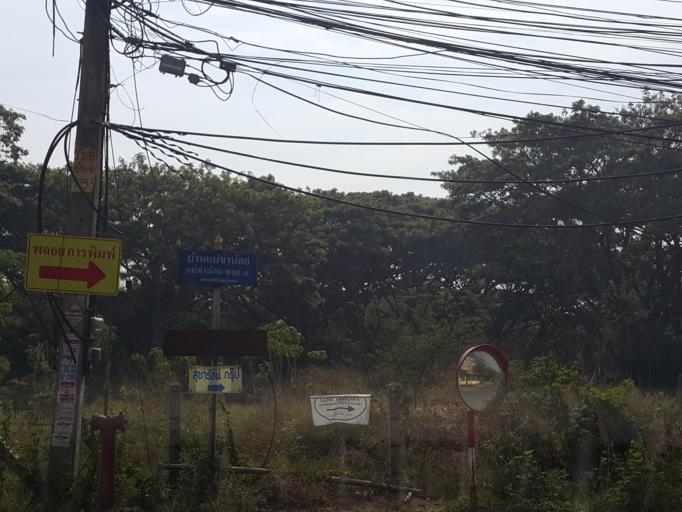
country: TH
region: Chiang Mai
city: Chiang Mai
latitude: 18.7623
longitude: 98.9812
